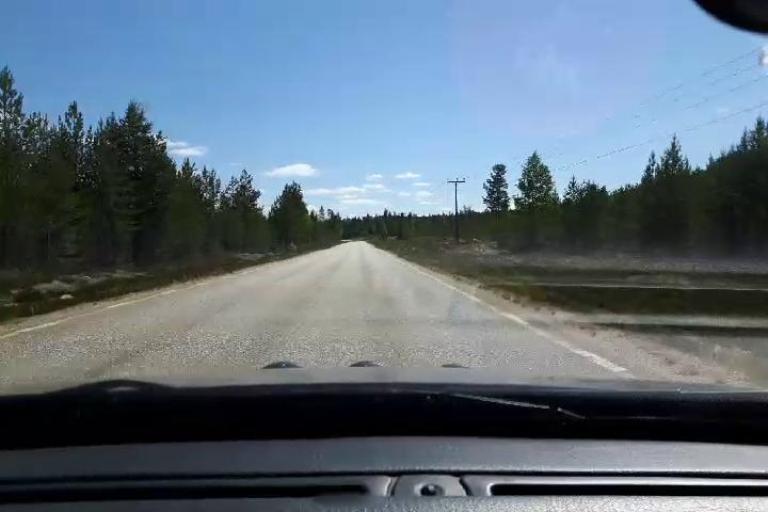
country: SE
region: Jaemtland
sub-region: Harjedalens Kommun
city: Sveg
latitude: 62.1063
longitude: 15.0654
